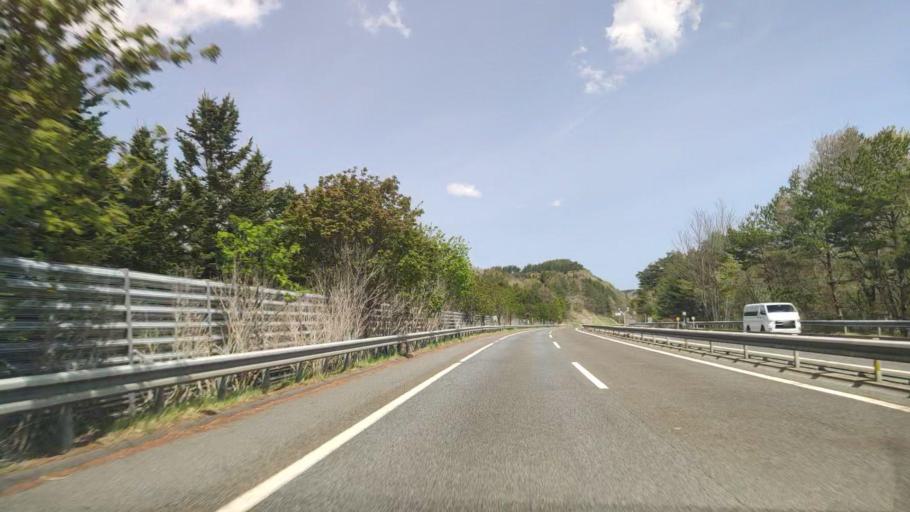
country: JP
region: Aomori
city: Hachinohe
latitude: 40.3501
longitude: 141.4478
